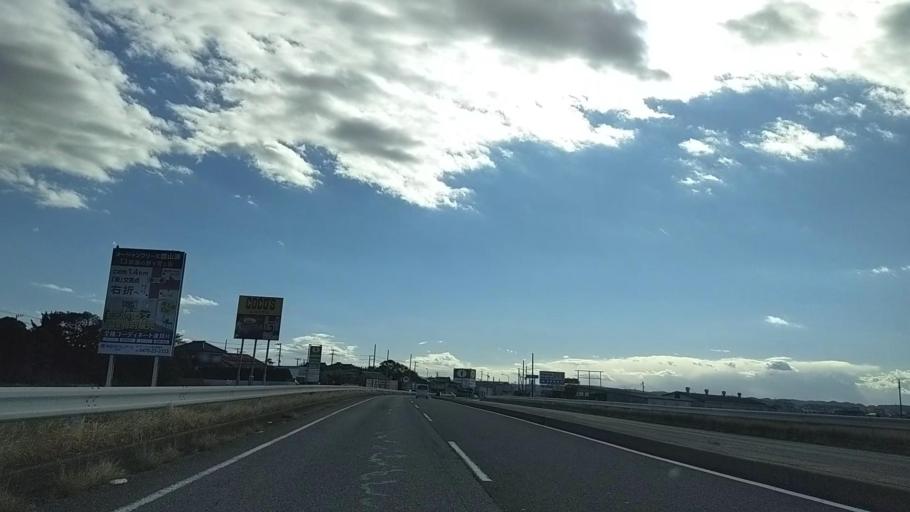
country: JP
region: Chiba
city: Tateyama
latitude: 35.0208
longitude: 139.8695
